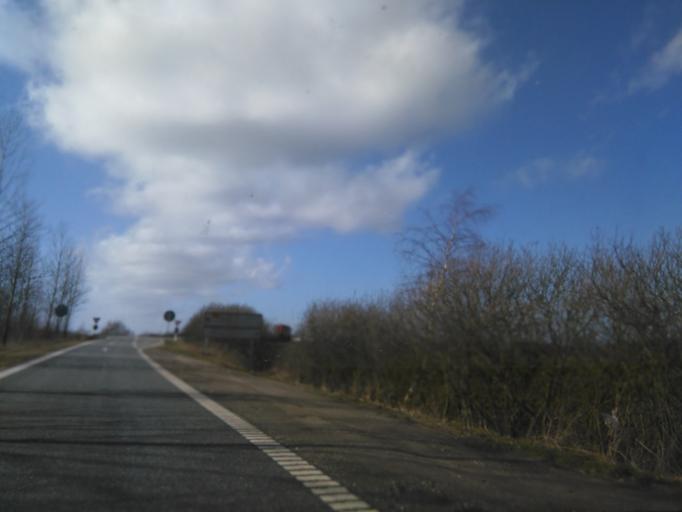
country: DK
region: South Denmark
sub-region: Nyborg Kommune
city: Nyborg
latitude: 55.3321
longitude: 10.7428
